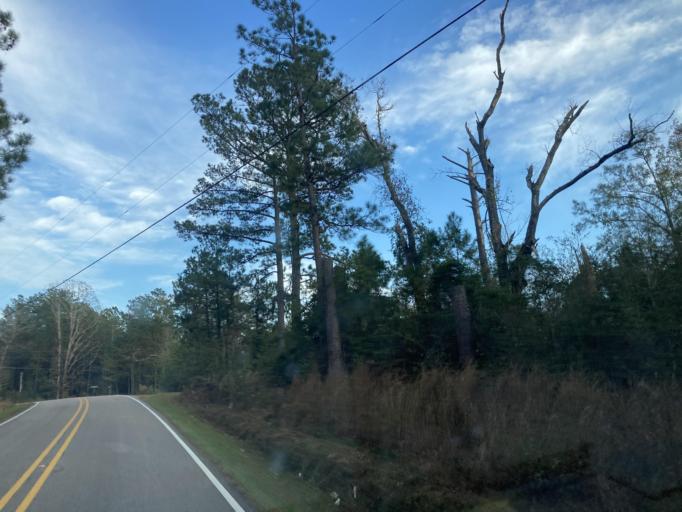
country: US
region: Mississippi
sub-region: Lamar County
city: Purvis
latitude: 31.1824
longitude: -89.3555
